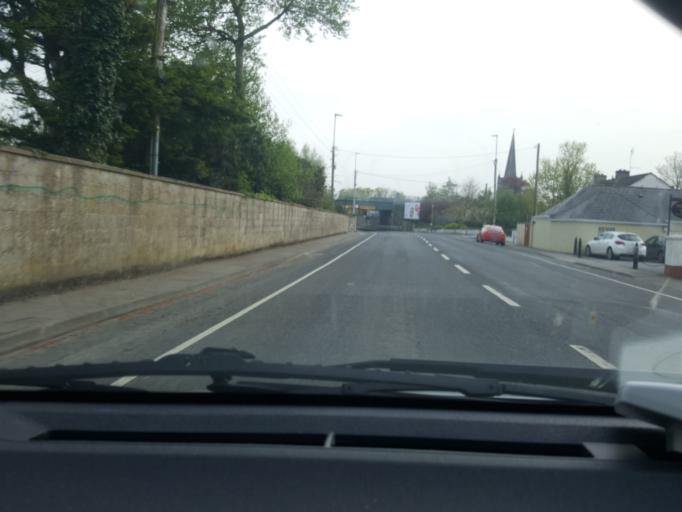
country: IE
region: Munster
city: Cahir
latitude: 52.3794
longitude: -7.9222
